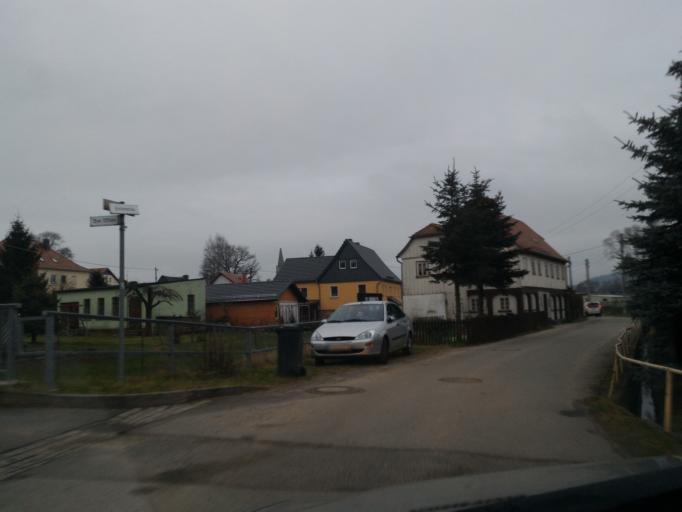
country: DE
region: Saxony
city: Leutersdorf
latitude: 50.9631
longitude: 14.6488
